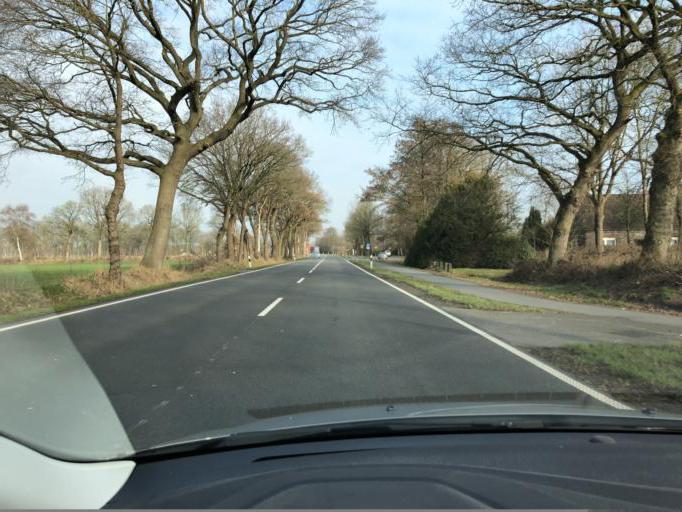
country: DE
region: Lower Saxony
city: Hesel
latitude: 53.3377
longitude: 7.6061
